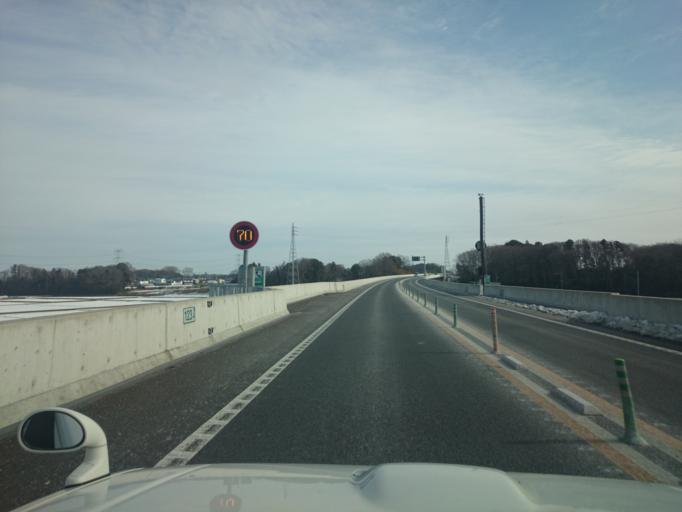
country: JP
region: Ibaraki
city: Sakai
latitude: 36.1271
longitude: 139.7878
